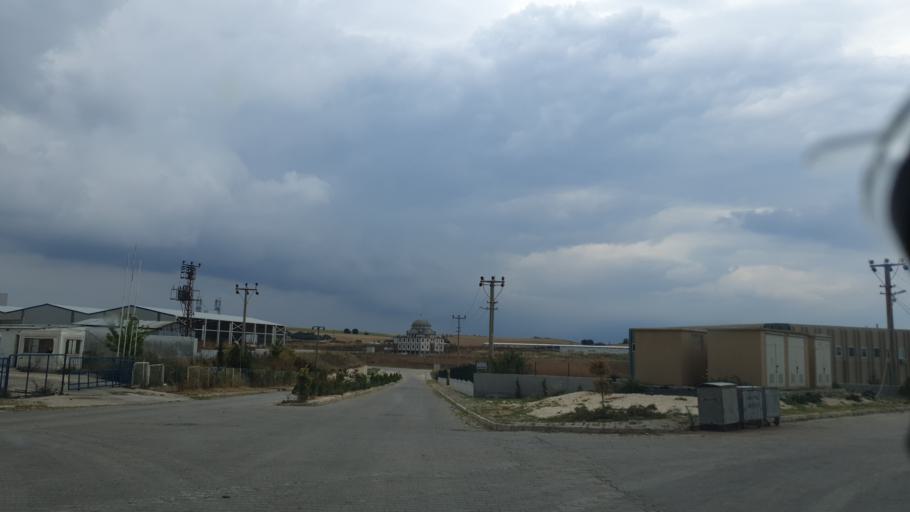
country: TR
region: Tekirdag
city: Hayrabolu
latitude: 41.2230
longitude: 27.0469
